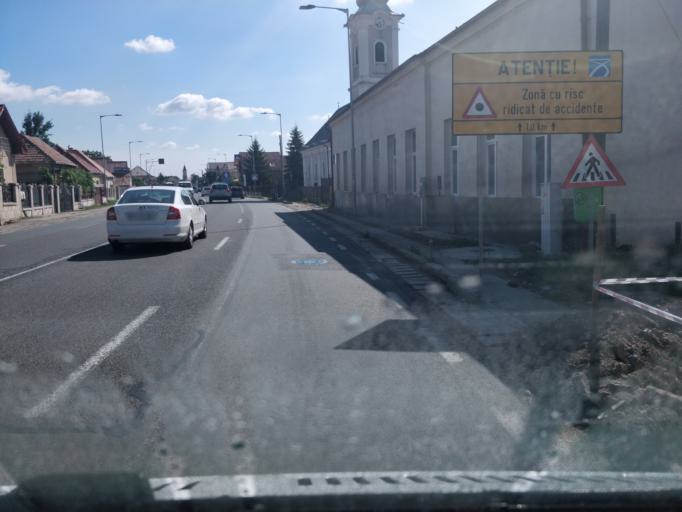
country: RO
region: Cluj
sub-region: Comuna Floresti
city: Floresti
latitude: 46.7437
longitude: 23.4782
